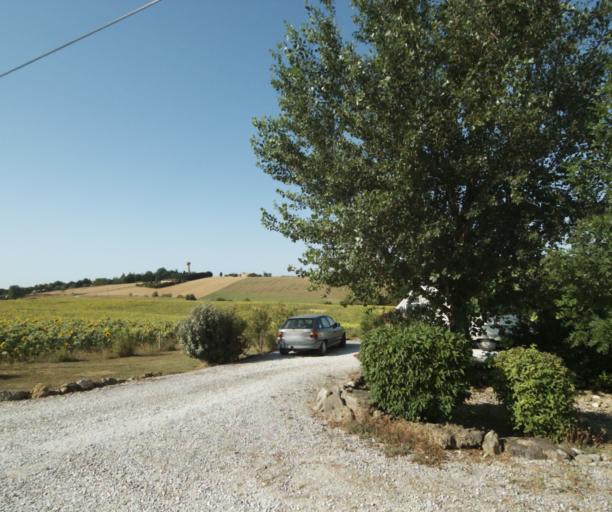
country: FR
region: Midi-Pyrenees
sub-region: Departement de la Haute-Garonne
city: Avignonet-Lauragais
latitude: 43.4195
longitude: 1.8201
